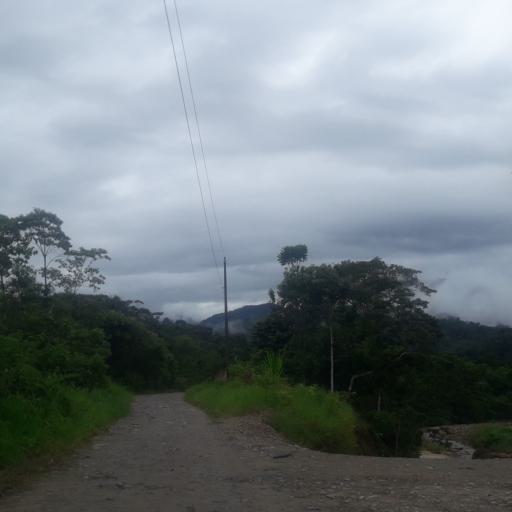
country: EC
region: Napo
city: Archidona
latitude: -0.9139
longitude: -77.8215
